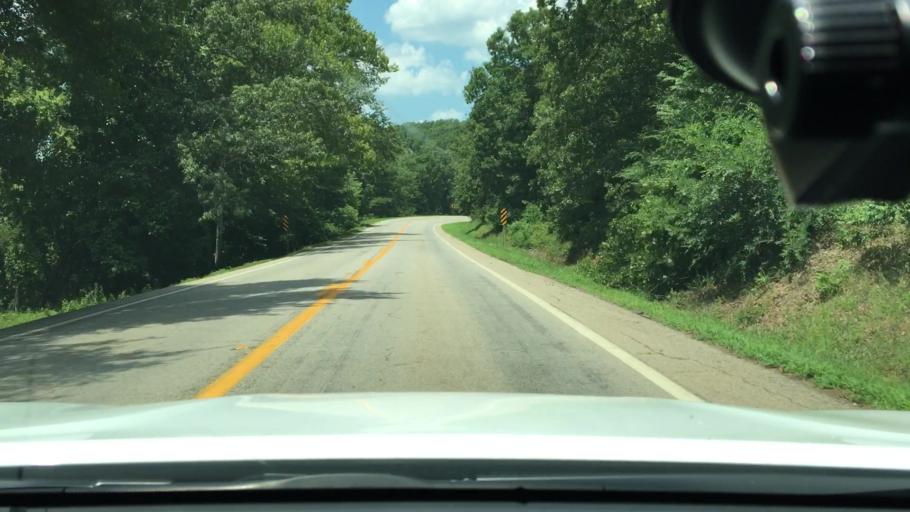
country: US
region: Arkansas
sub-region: Logan County
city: Booneville
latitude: 35.2135
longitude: -93.9378
